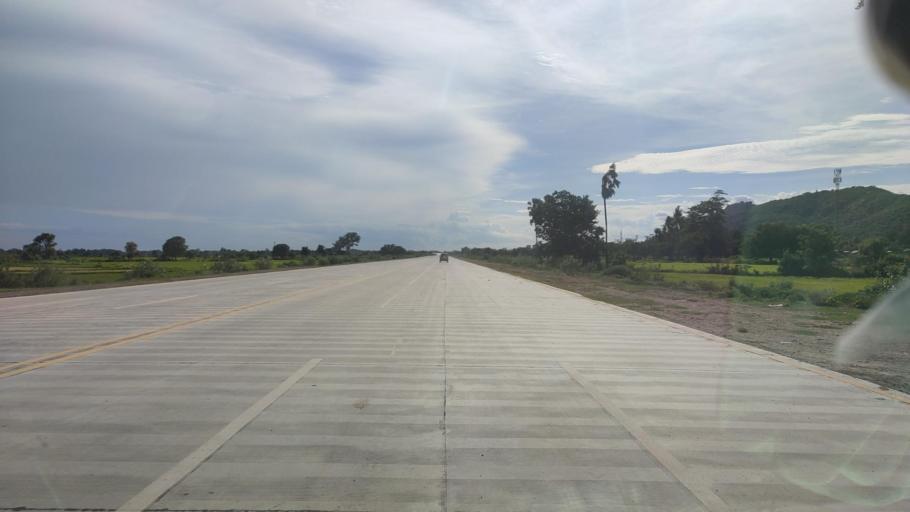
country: MM
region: Mandalay
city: Kyaukse
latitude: 21.5981
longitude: 96.1726
